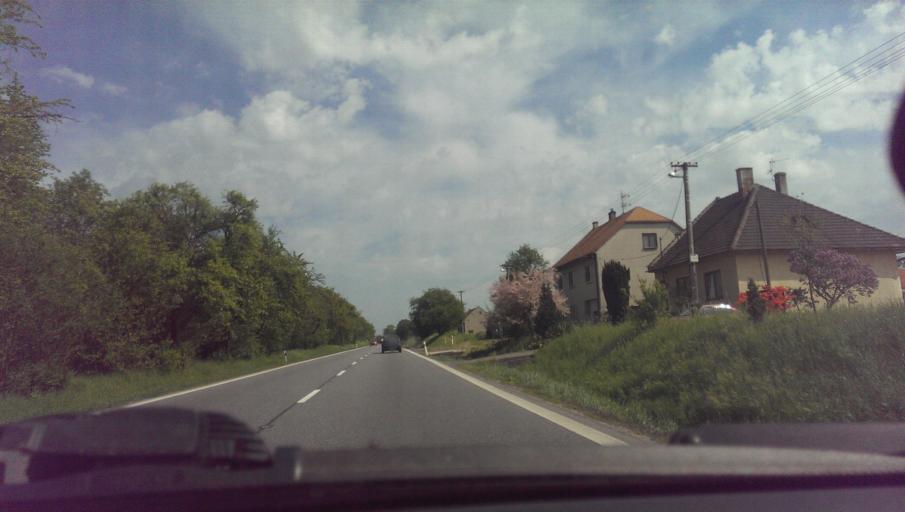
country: CZ
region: Zlin
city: Spytihnev
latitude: 49.1487
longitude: 17.5014
